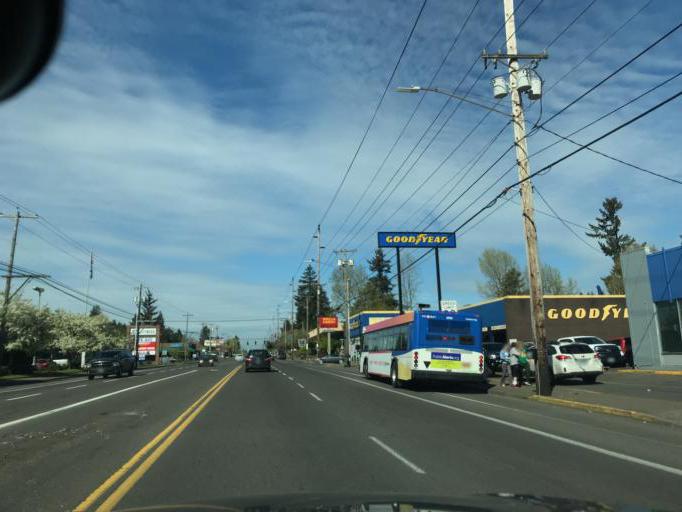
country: US
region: Oregon
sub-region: Multnomah County
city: Lents
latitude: 45.5041
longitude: -122.5378
